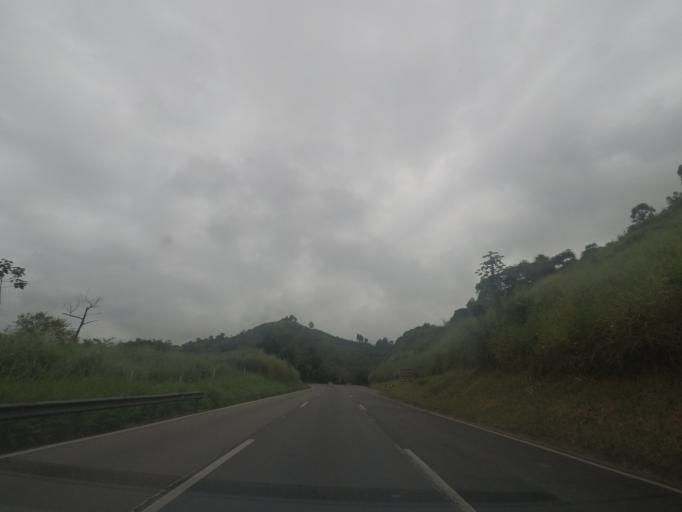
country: BR
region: Sao Paulo
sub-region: Cajati
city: Cajati
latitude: -24.8399
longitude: -48.2201
